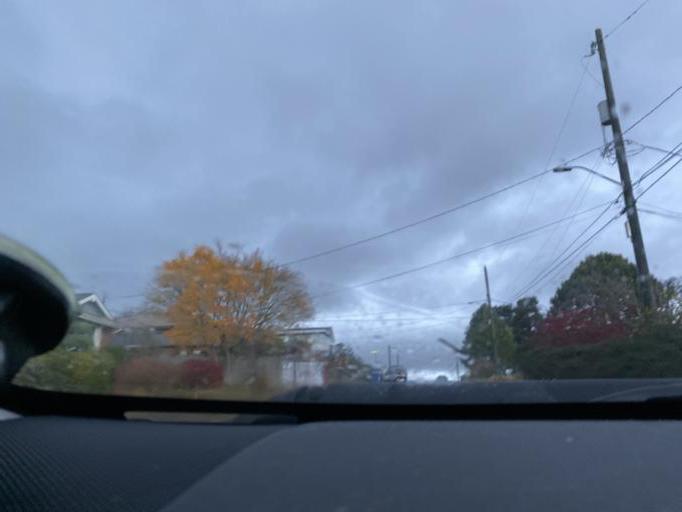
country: US
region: Washington
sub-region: King County
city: Seattle
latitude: 47.6417
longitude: -122.3903
